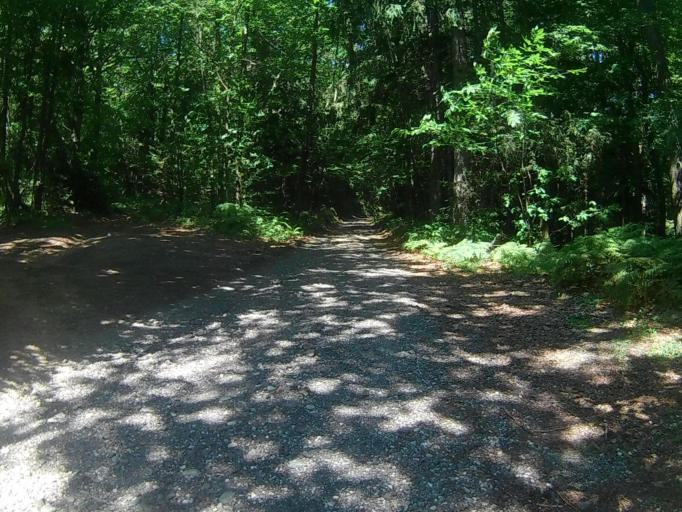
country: SI
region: Race-Fram
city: Fram
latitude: 46.4725
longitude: 15.6267
